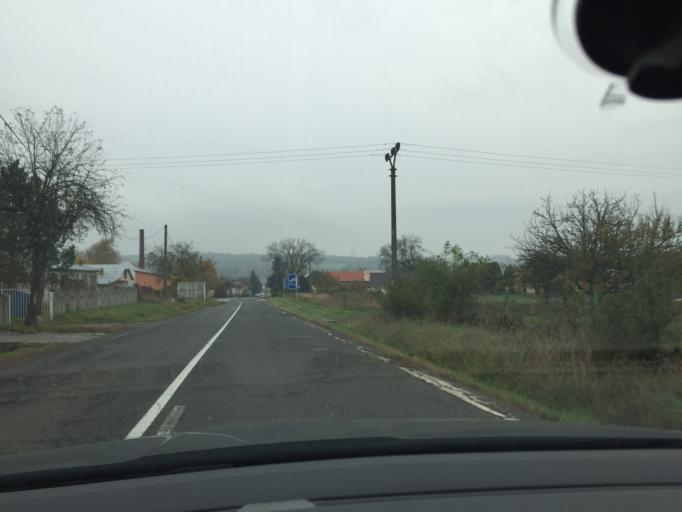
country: SK
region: Banskobystricky
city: Velky Krtis
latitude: 48.2361
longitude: 19.4223
